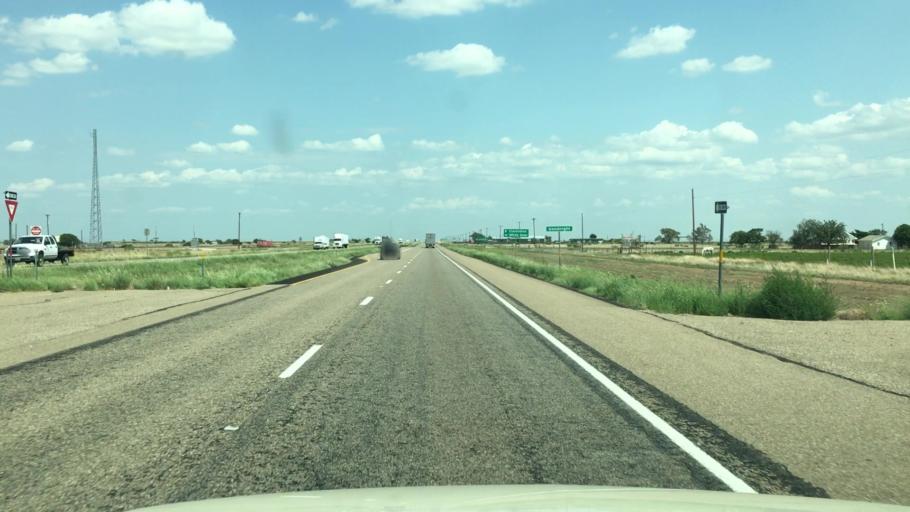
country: US
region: Texas
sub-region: Armstrong County
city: Claude
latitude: 35.0341
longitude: -101.1893
